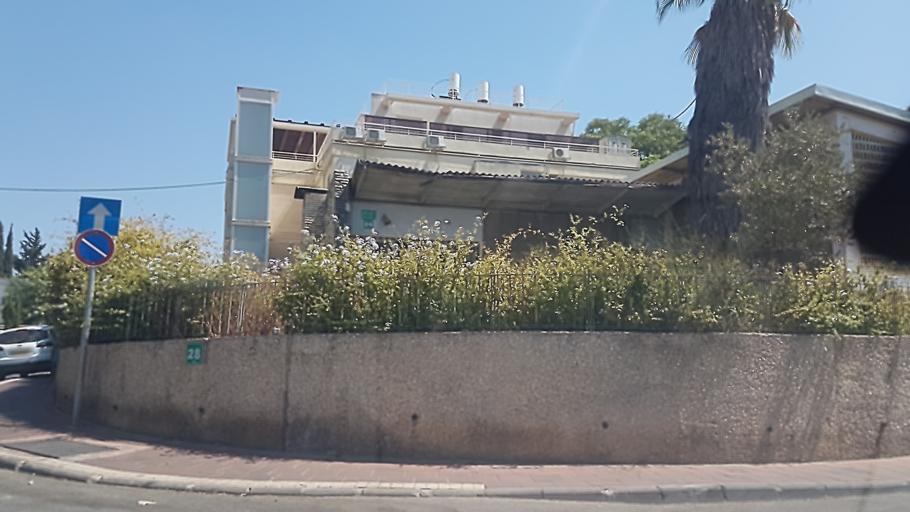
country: IL
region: Tel Aviv
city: Bene Beraq
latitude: 32.0826
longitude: 34.8244
